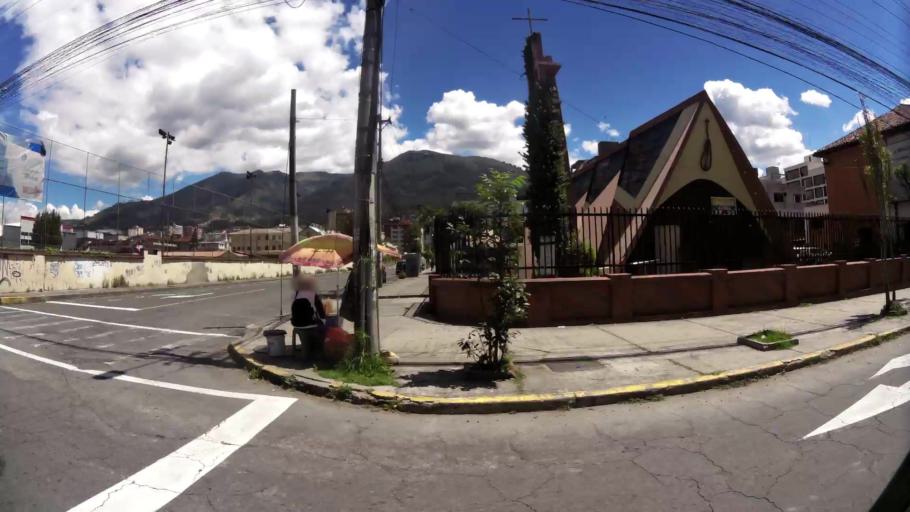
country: EC
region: Pichincha
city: Quito
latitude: -0.1718
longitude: -78.4877
